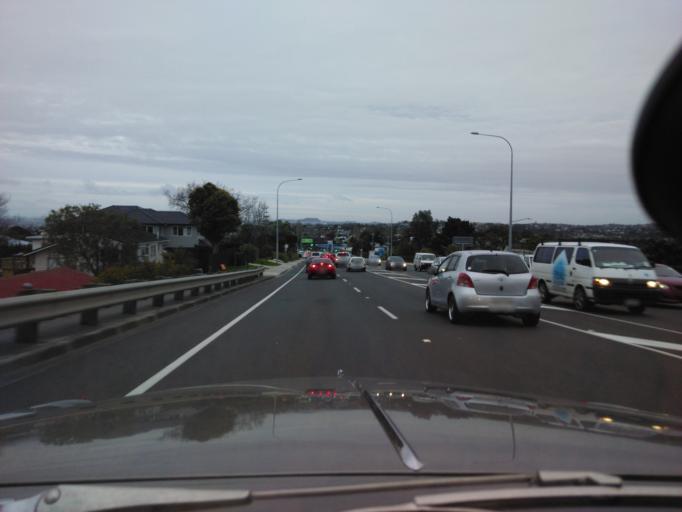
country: NZ
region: Auckland
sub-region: Auckland
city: Rothesay Bay
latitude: -36.7662
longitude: 174.7195
